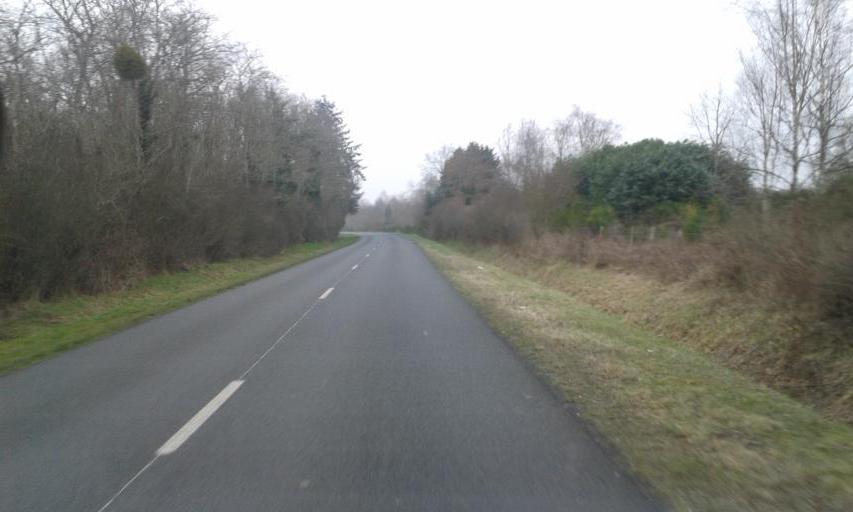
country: FR
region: Centre
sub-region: Departement du Loiret
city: Lailly-en-Val
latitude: 47.7266
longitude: 1.6551
